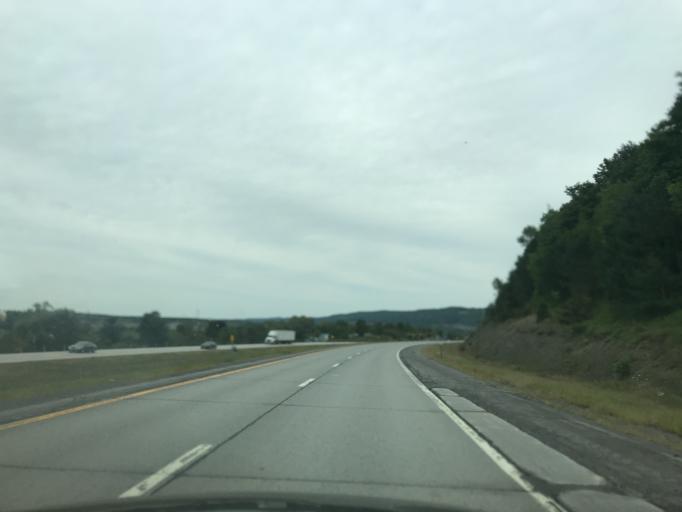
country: US
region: New York
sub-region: Schoharie County
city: Cobleskill
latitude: 42.6797
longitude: -74.4125
